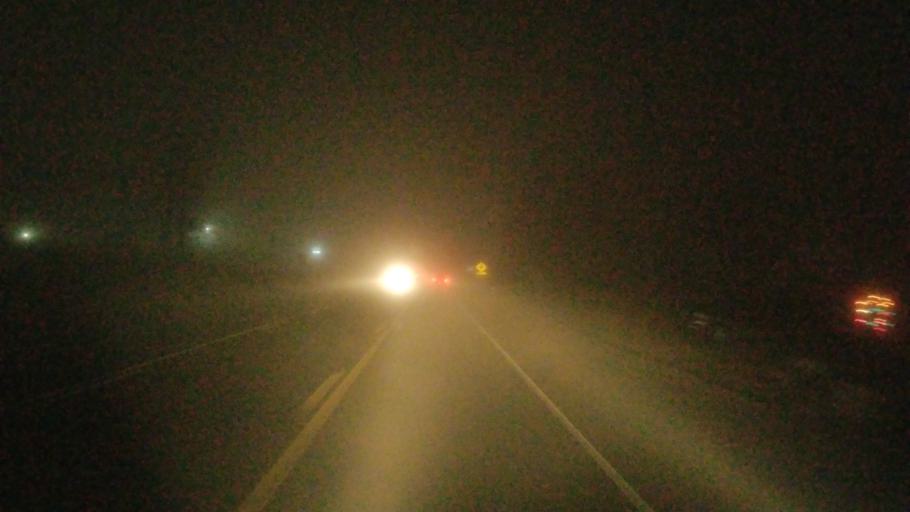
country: US
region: Pennsylvania
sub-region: Butler County
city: Prospect
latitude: 40.9095
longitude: -80.0343
